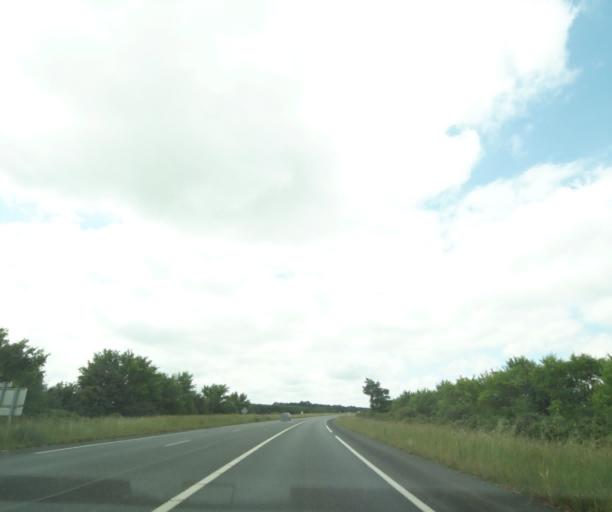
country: FR
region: Poitou-Charentes
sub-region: Departement des Deux-Sevres
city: Saint-Varent
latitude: 46.8727
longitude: -0.1980
